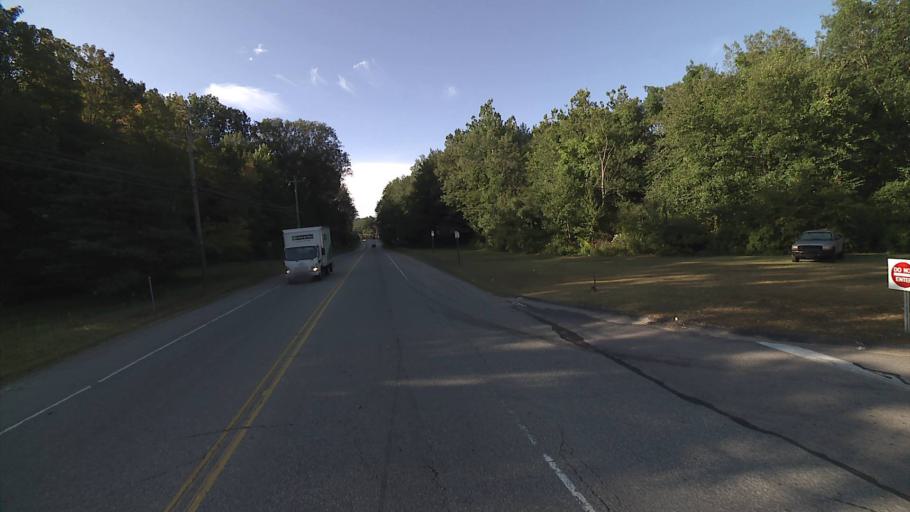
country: US
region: Connecticut
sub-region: New London County
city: Baltic
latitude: 41.5742
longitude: -72.1319
